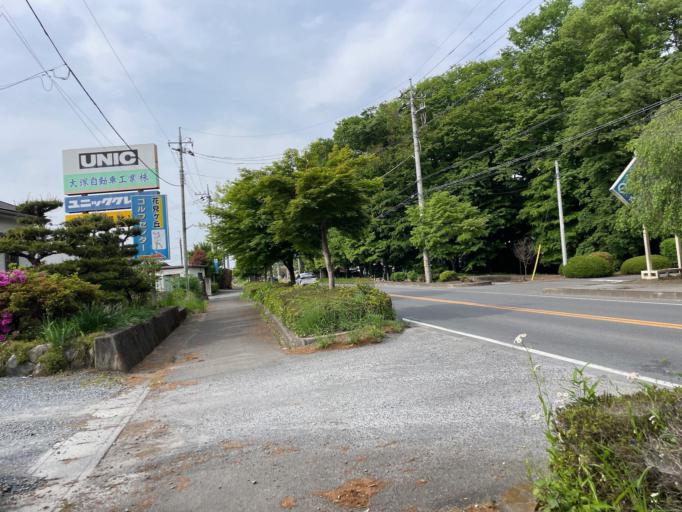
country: JP
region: Tochigi
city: Mibu
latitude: 36.3996
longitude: 139.8035
